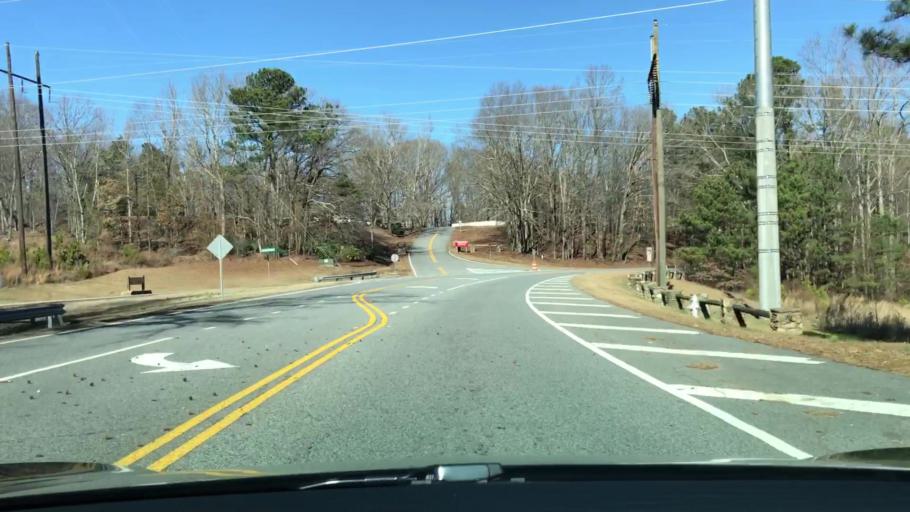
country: US
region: Georgia
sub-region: Gwinnett County
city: Sugar Hill
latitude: 34.1549
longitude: -84.0708
